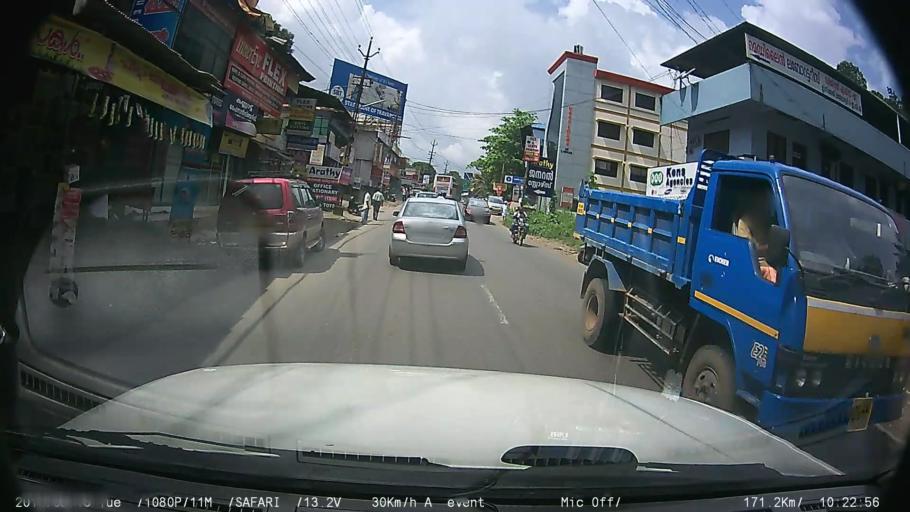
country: IN
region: Kerala
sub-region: Kottayam
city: Kottayam
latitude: 9.6677
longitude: 76.5548
